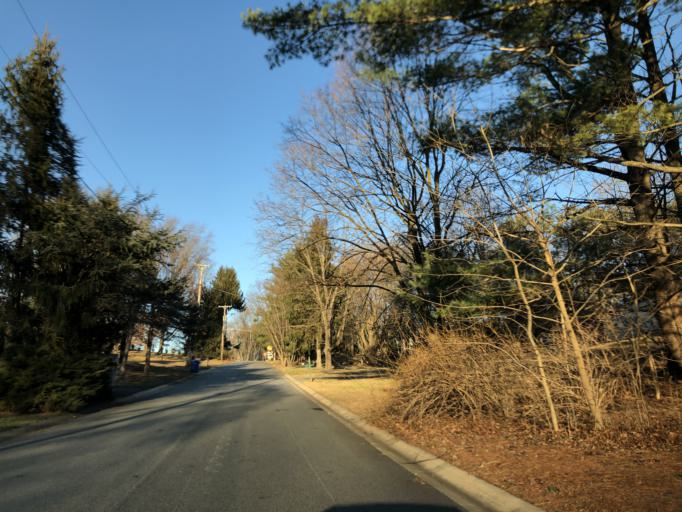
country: US
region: Pennsylvania
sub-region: Delaware County
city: Chester Heights
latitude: 39.8669
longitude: -75.4966
